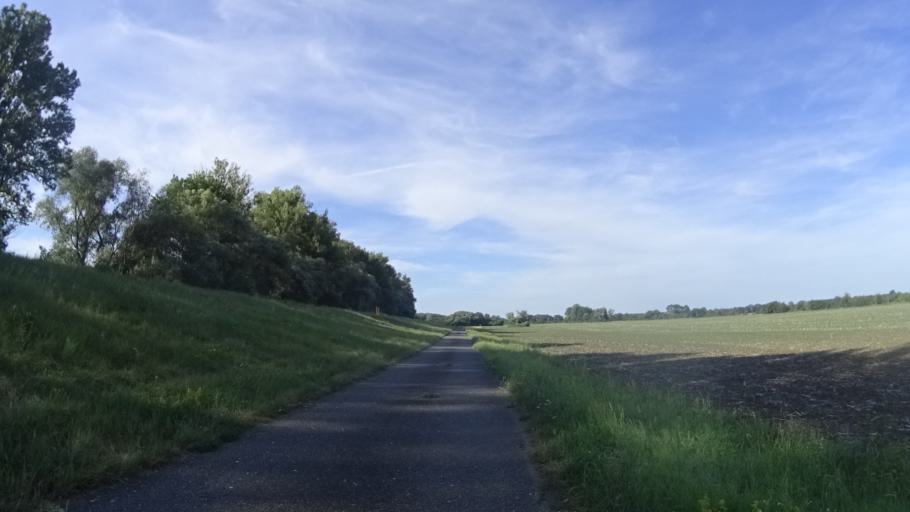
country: AT
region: Lower Austria
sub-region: Politischer Bezirk Ganserndorf
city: Drosing
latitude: 48.5270
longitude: 16.9555
